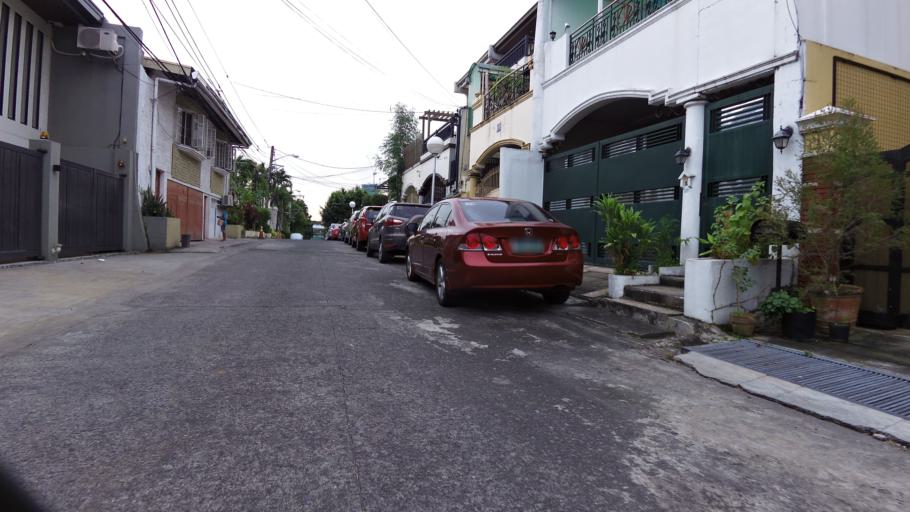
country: PH
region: Metro Manila
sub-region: Pasig
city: Pasig City
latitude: 14.5690
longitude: 121.0617
